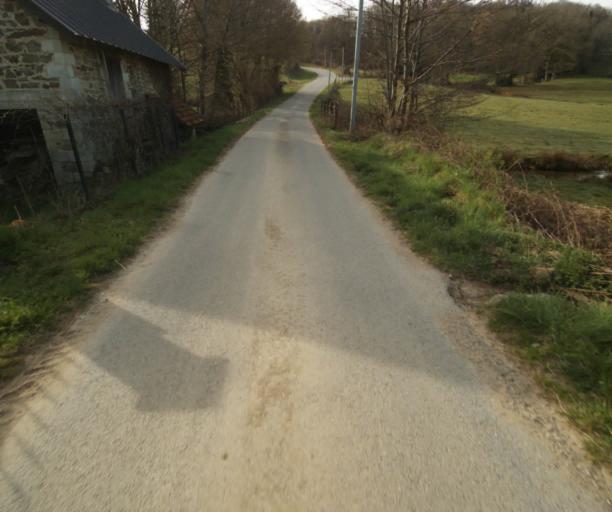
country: FR
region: Limousin
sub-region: Departement de la Correze
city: Chamboulive
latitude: 45.4442
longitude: 1.7537
